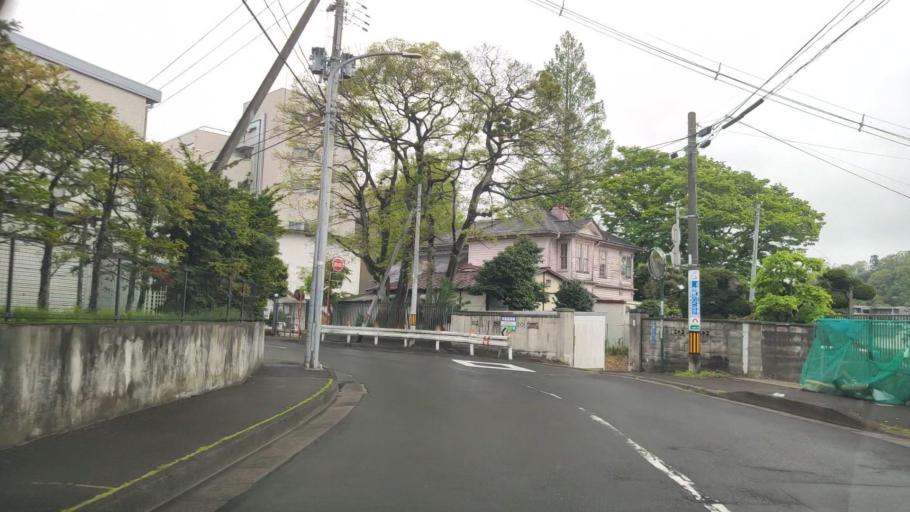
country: JP
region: Miyagi
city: Sendai
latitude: 38.2503
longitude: 140.8753
